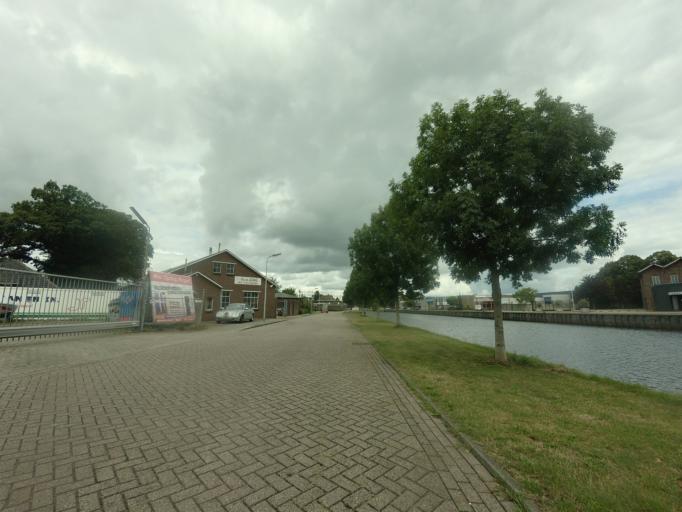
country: NL
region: Drenthe
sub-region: Gemeente Meppel
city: Meppel
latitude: 52.7029
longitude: 6.1852
